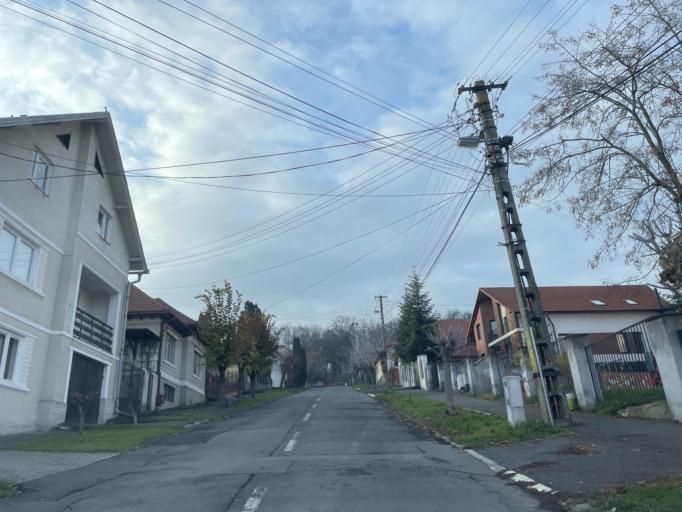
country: RO
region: Mures
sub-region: Municipiul Reghin
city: Reghin
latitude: 46.7820
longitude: 24.6942
